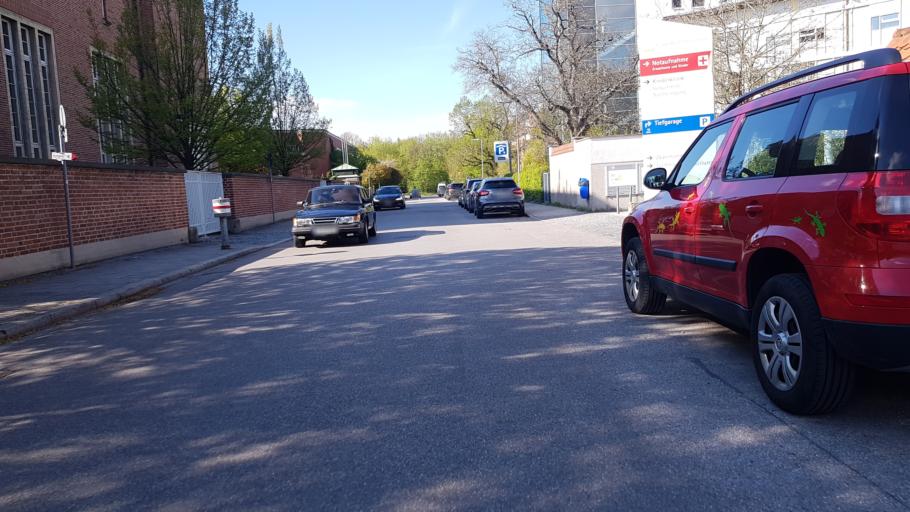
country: DE
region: Bavaria
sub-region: Upper Bavaria
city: Pasing
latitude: 48.1657
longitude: 11.5029
